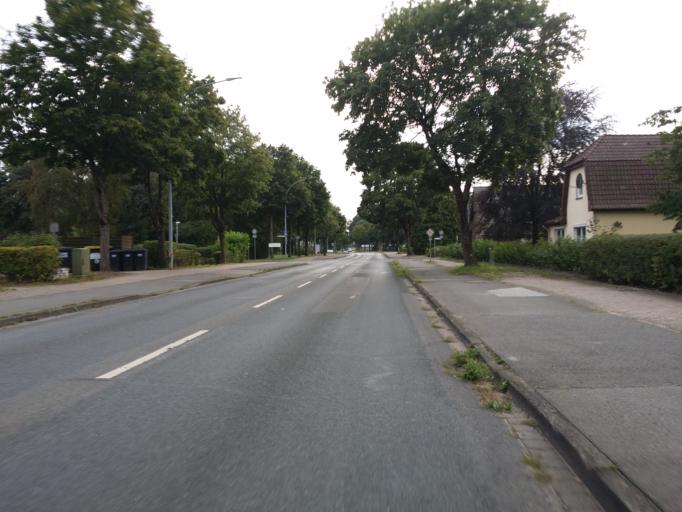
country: DE
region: Lower Saxony
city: Bremervorde
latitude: 53.4740
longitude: 9.1347
